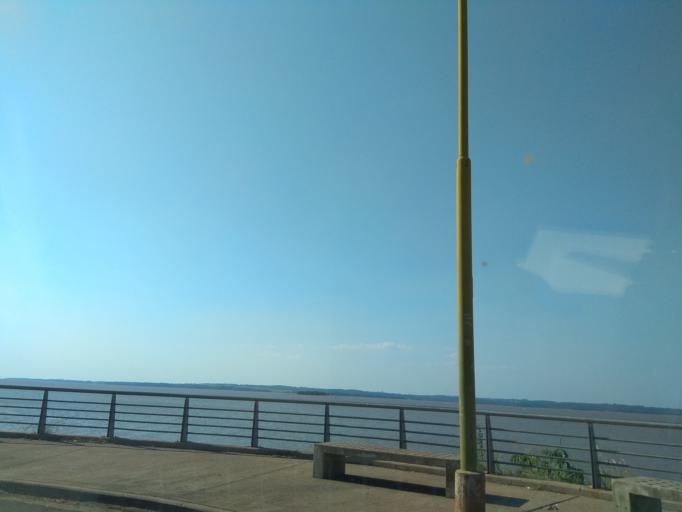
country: AR
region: Misiones
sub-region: Departamento de Capital
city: Posadas
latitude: -27.3532
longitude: -55.9411
